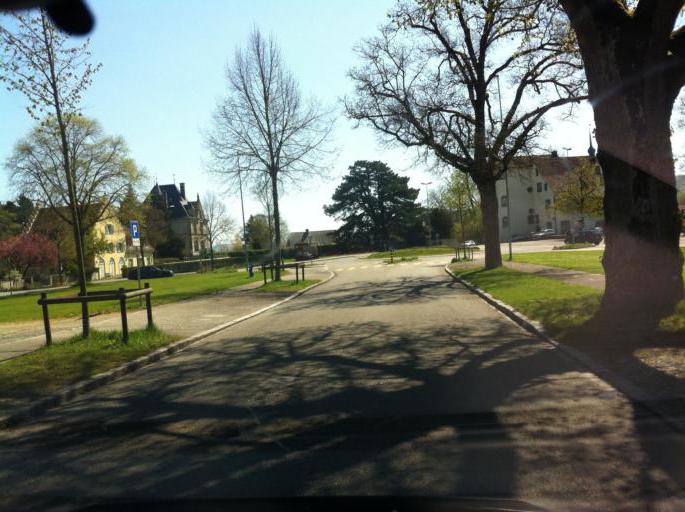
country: CH
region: Schaffhausen
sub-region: Bezirk Schaffhausen
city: Schaffhausen
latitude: 47.7007
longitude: 8.6254
